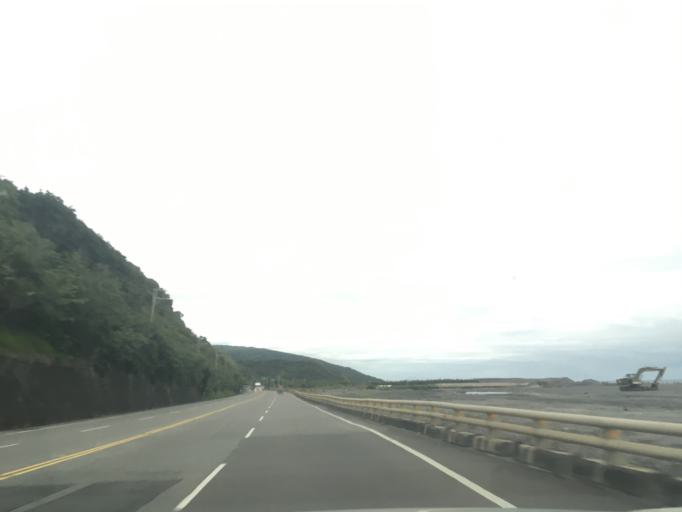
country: TW
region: Taiwan
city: Hengchun
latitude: 22.3321
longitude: 120.8933
